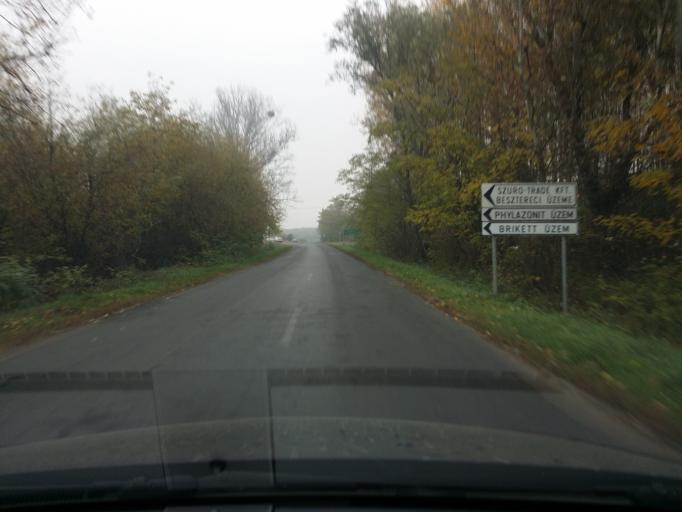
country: HU
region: Szabolcs-Szatmar-Bereg
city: Kek
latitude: 48.0956
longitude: 21.8817
